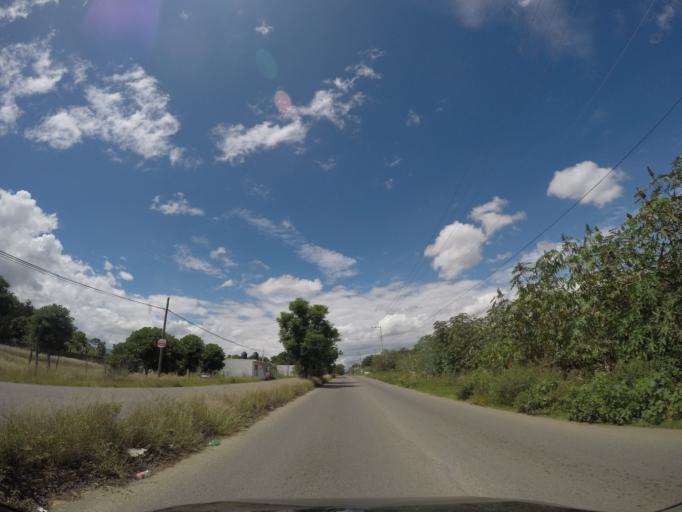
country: MX
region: Oaxaca
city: San Raymundo Jalpam
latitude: 16.9753
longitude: -96.7499
